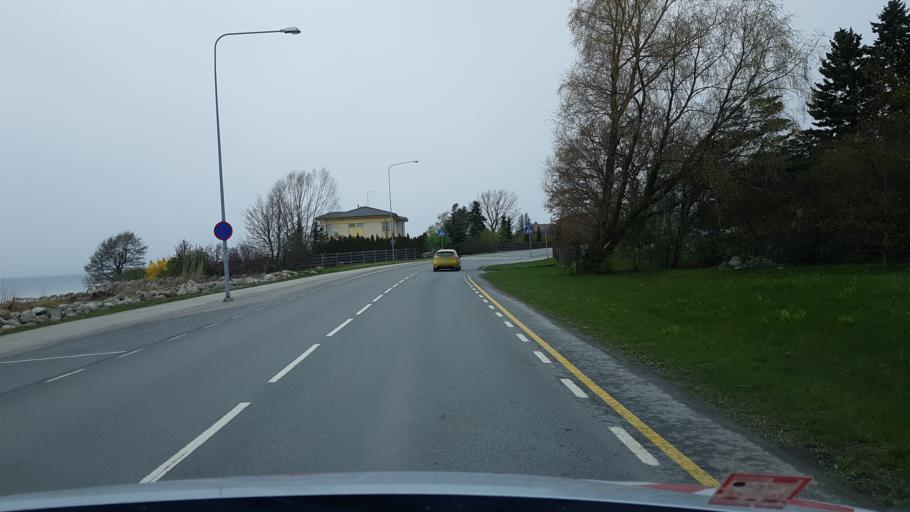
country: EE
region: Harju
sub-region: Viimsi vald
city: Rummu
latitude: 59.5542
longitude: 24.7940
